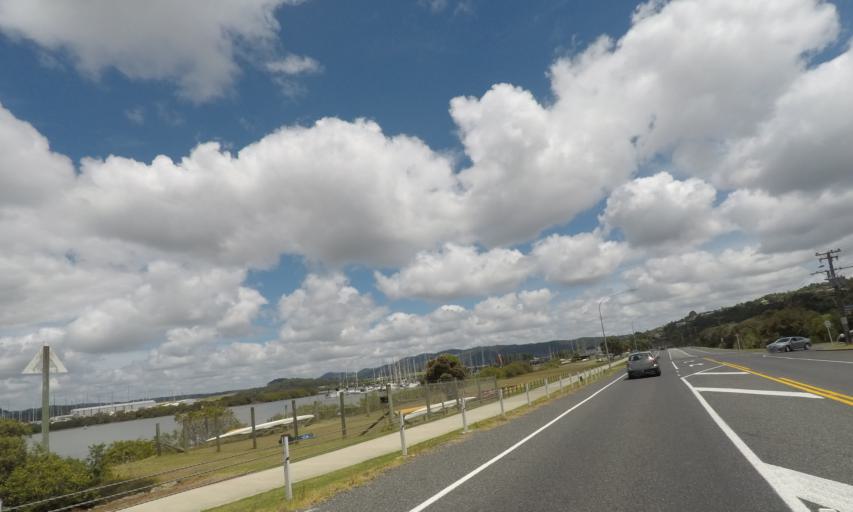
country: NZ
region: Northland
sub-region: Whangarei
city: Whangarei
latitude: -35.7362
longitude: 174.3520
